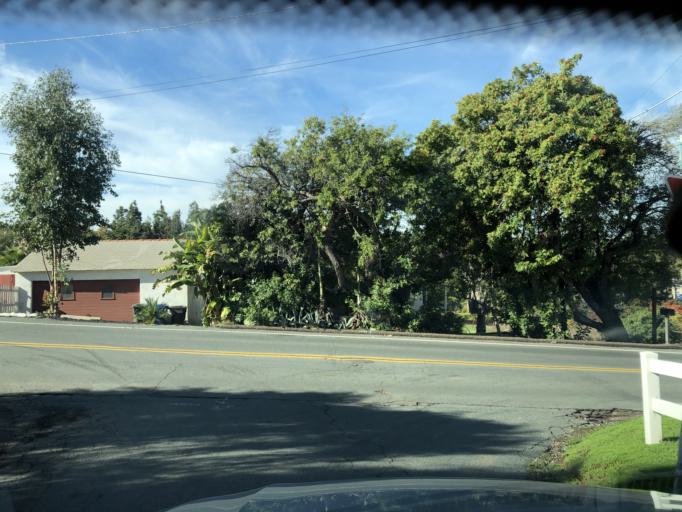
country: US
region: California
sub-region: San Diego County
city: Chula Vista
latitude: 32.6453
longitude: -117.0615
